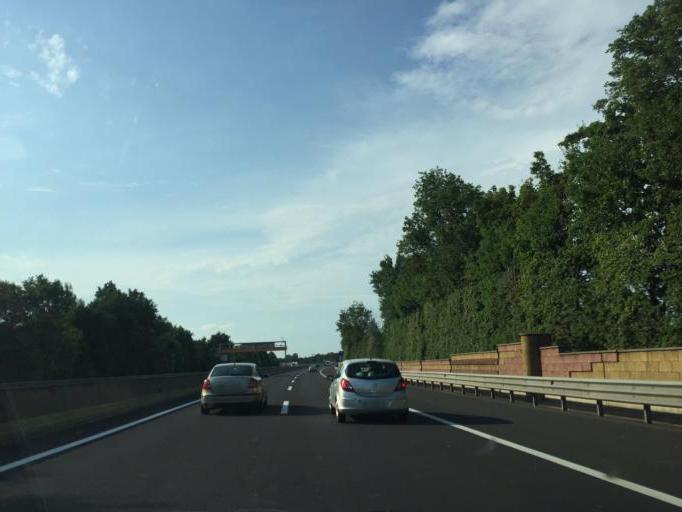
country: AT
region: Styria
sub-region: Politischer Bezirk Leibnitz
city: Weitendorf
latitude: 46.8863
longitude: 15.4735
